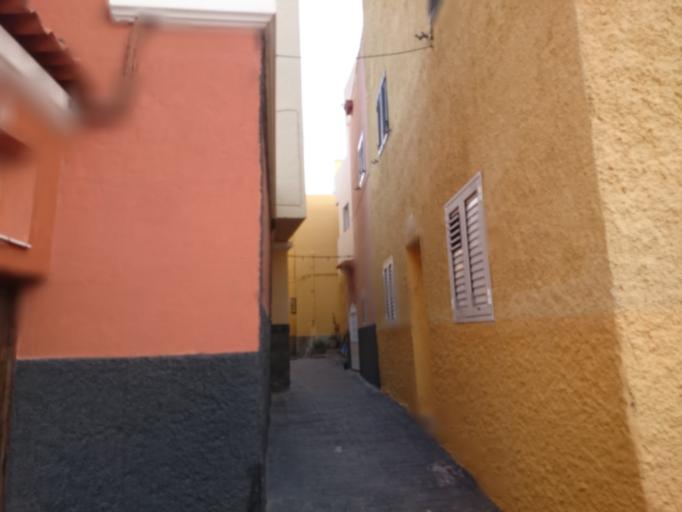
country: ES
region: Canary Islands
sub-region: Provincia de Las Palmas
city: Firgas
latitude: 28.1445
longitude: -15.5733
